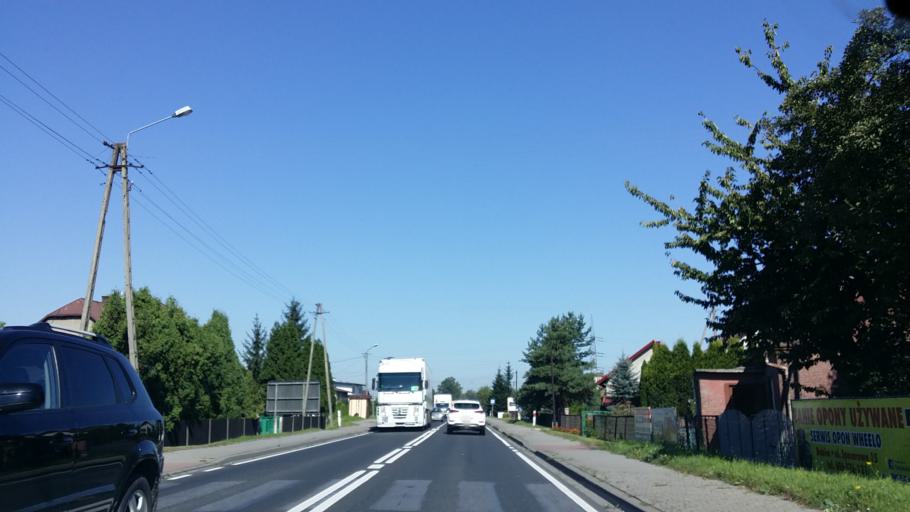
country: PL
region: Lesser Poland Voivodeship
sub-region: Powiat oswiecimski
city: Babice
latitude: 50.0555
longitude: 19.1995
